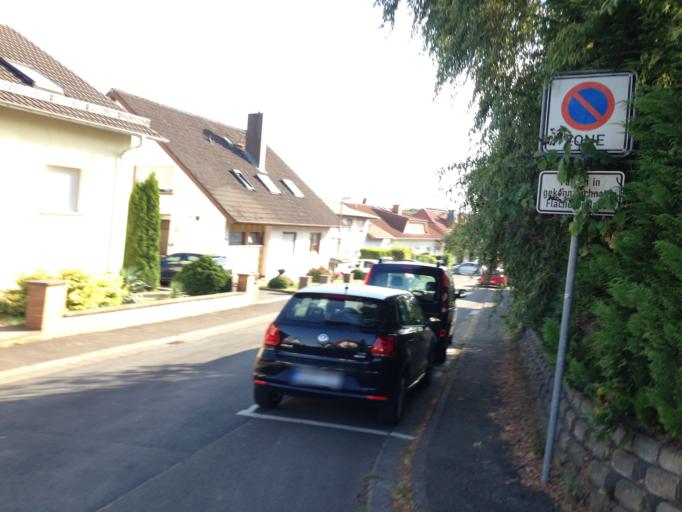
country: DE
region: Hesse
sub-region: Regierungsbezirk Giessen
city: Reiskirchen
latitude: 50.6197
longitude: 8.8505
